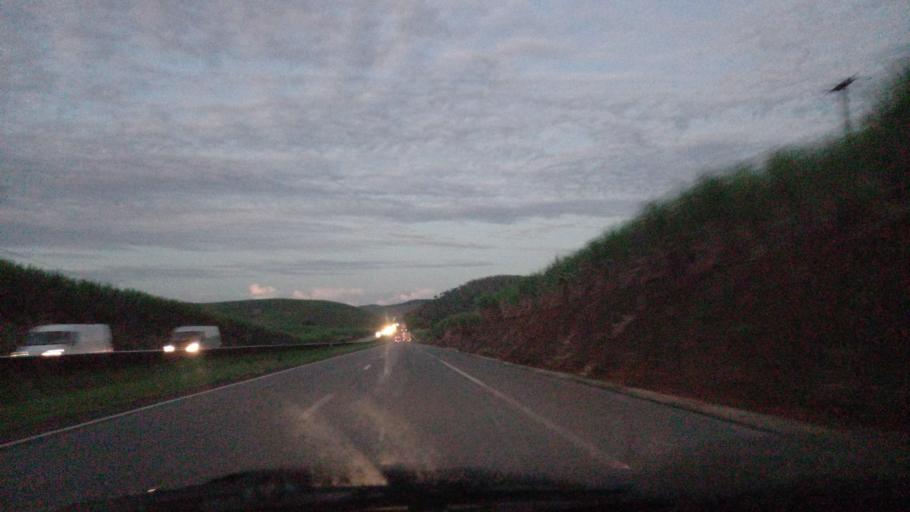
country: BR
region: Pernambuco
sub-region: Escada
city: Escada
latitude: -8.4115
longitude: -35.2948
